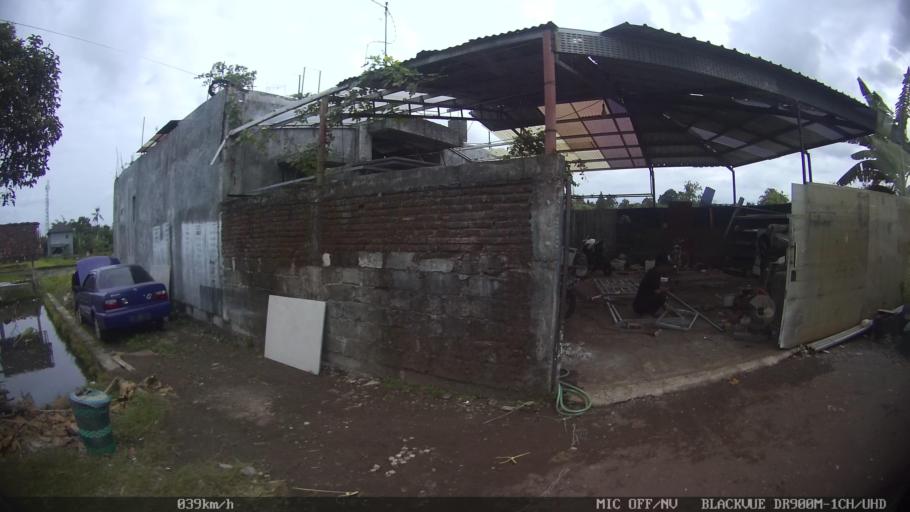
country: ID
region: Daerah Istimewa Yogyakarta
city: Depok
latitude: -7.8347
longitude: 110.4207
